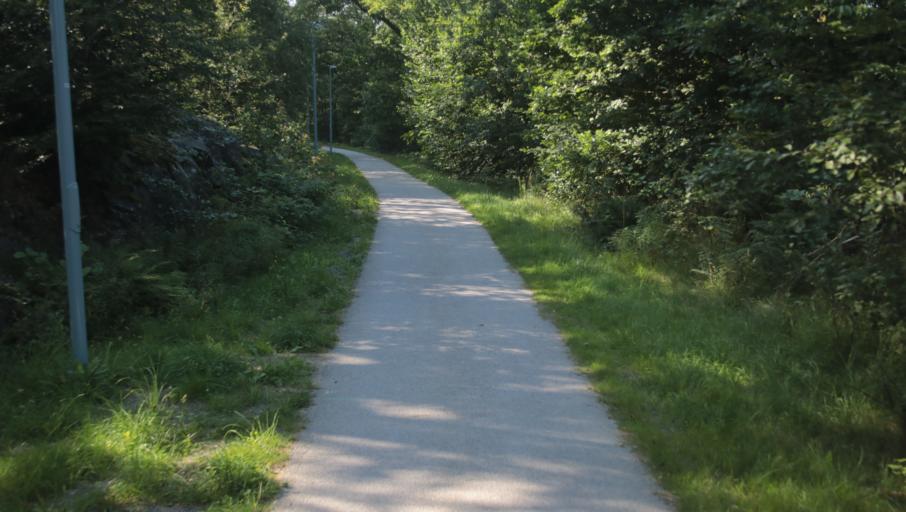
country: SE
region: Blekinge
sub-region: Karlshamns Kommun
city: Svangsta
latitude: 56.2539
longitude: 14.7881
